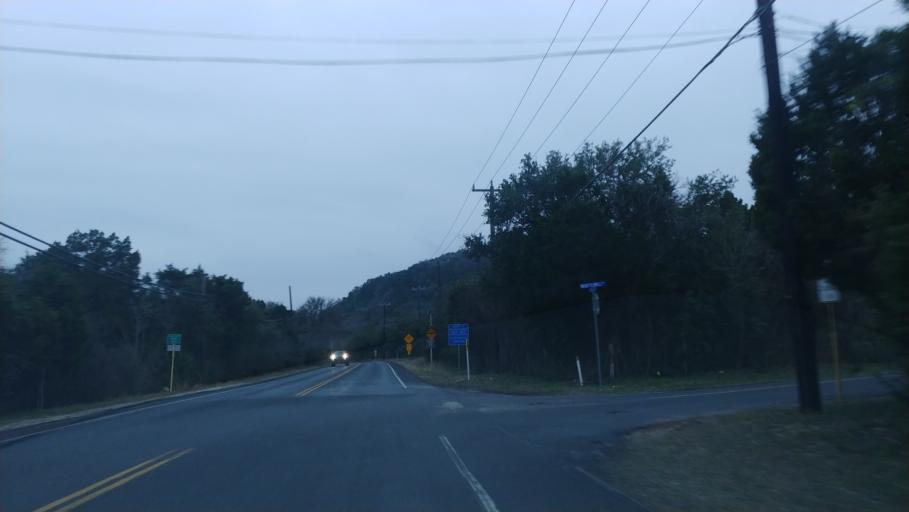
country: US
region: Texas
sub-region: Bexar County
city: Helotes
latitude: 29.5912
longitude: -98.6891
